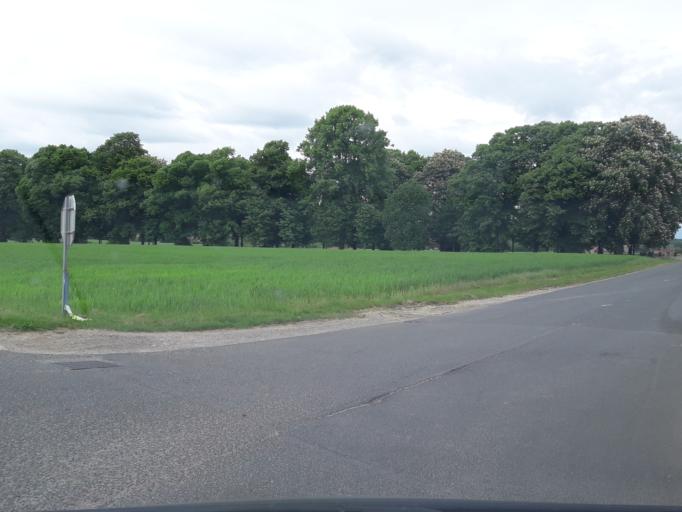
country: FR
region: Ile-de-France
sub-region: Departement de l'Essonne
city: Boissy-le-Cutte
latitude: 48.4253
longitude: 2.2835
